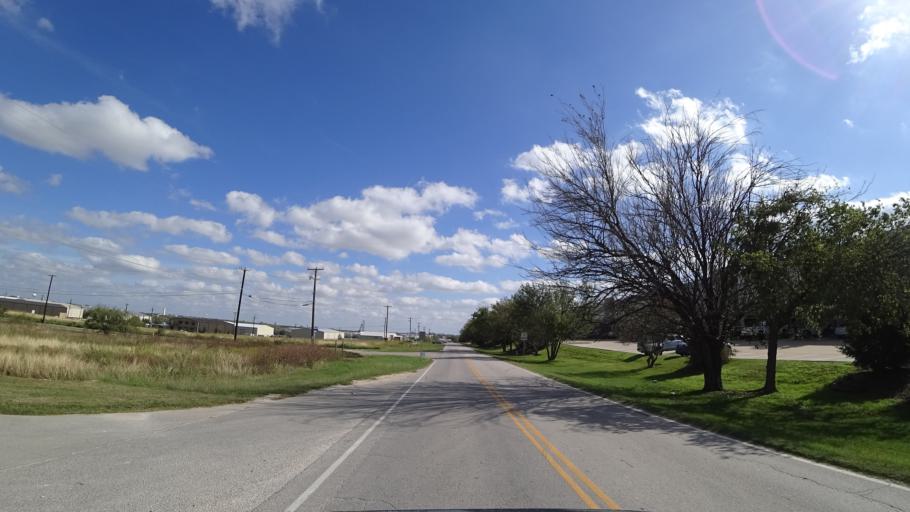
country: US
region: Texas
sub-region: Travis County
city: Windemere
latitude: 30.4686
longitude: -97.6665
